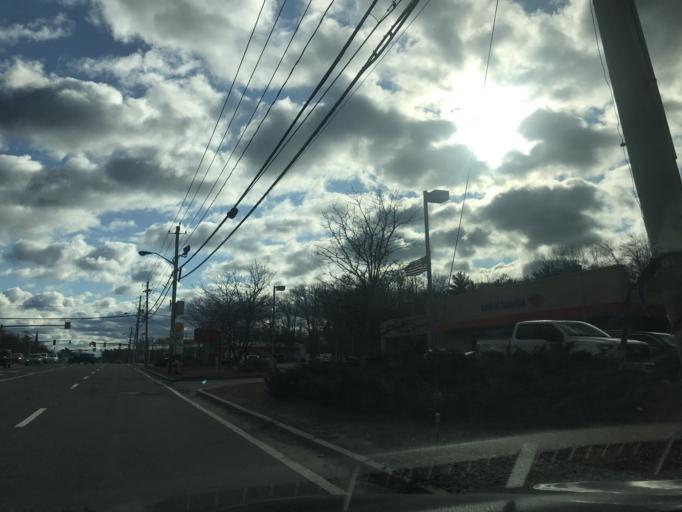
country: US
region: Massachusetts
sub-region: Plymouth County
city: Hanover
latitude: 42.1468
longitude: -70.8455
